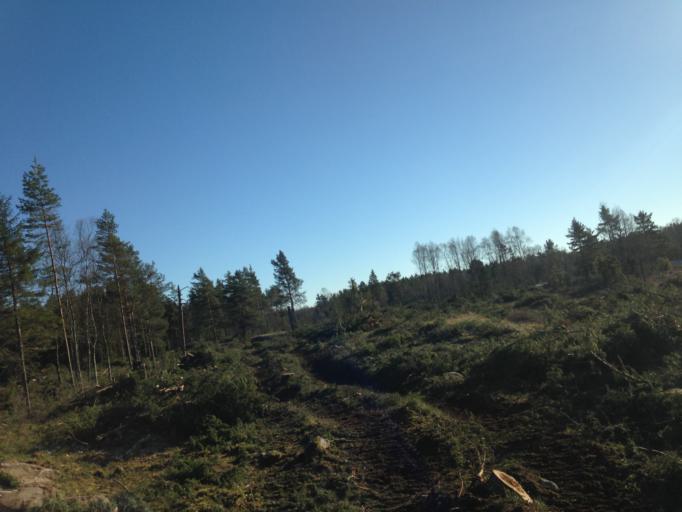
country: SE
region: Soedermanland
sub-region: Nykopings Kommun
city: Svalsta
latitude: 58.4872
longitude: 16.8759
